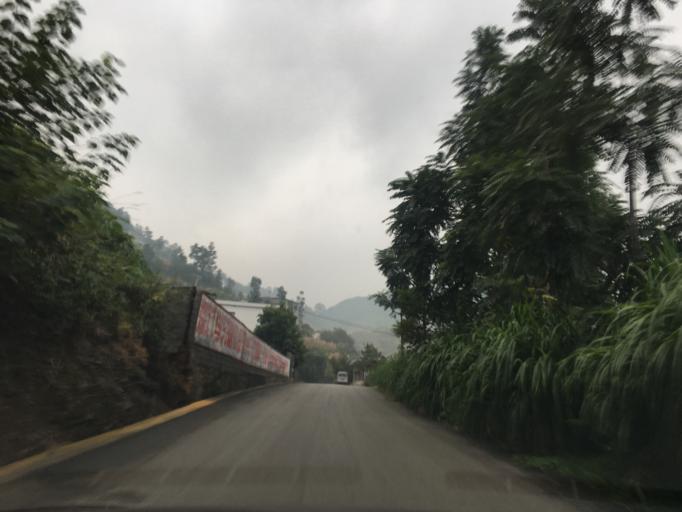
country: CN
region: Guizhou Sheng
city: Liupanshui
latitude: 26.0646
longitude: 105.1385
